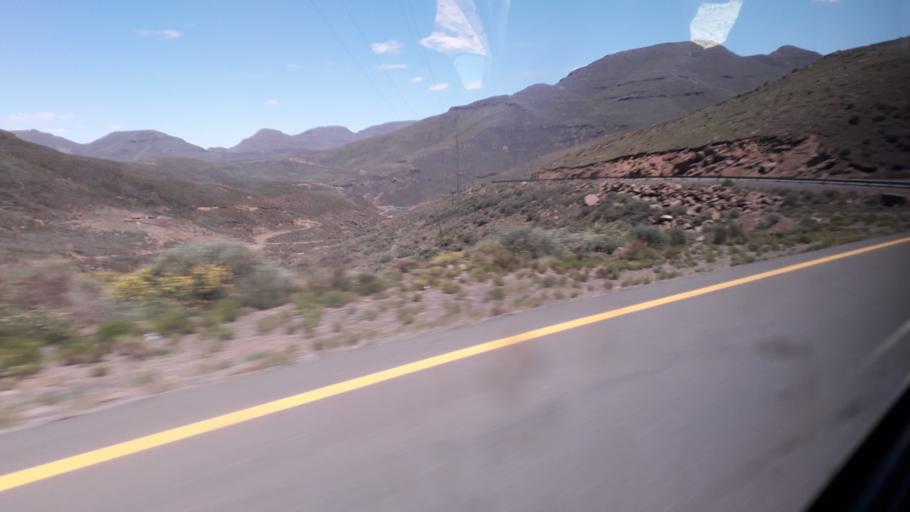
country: ZA
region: Orange Free State
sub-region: Thabo Mofutsanyana District Municipality
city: Phuthaditjhaba
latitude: -28.7701
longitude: 28.6656
